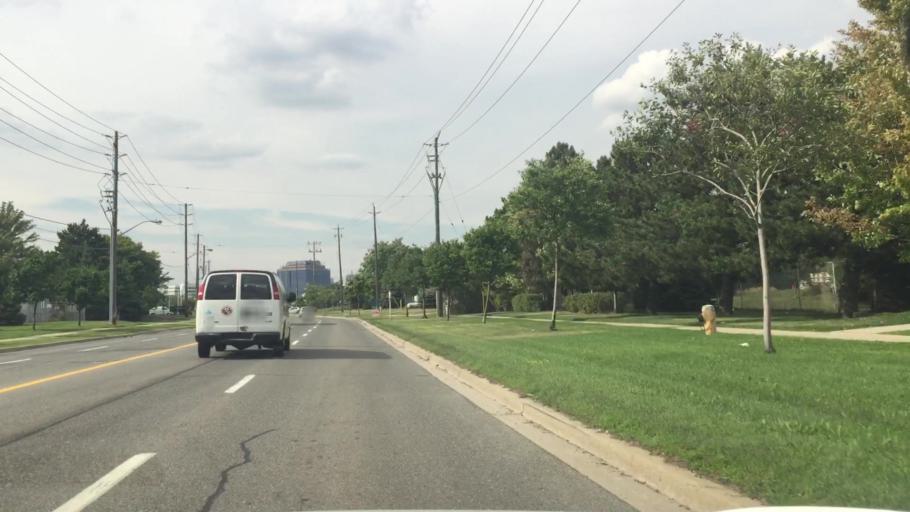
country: CA
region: Ontario
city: Concord
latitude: 43.7632
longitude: -79.5402
